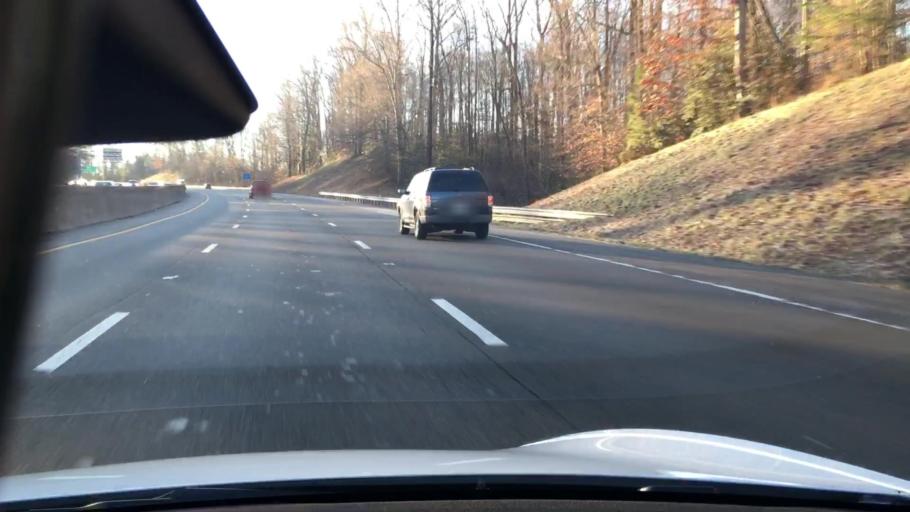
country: US
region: Virginia
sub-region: Chesterfield County
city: Bensley
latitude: 37.4554
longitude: -77.4941
